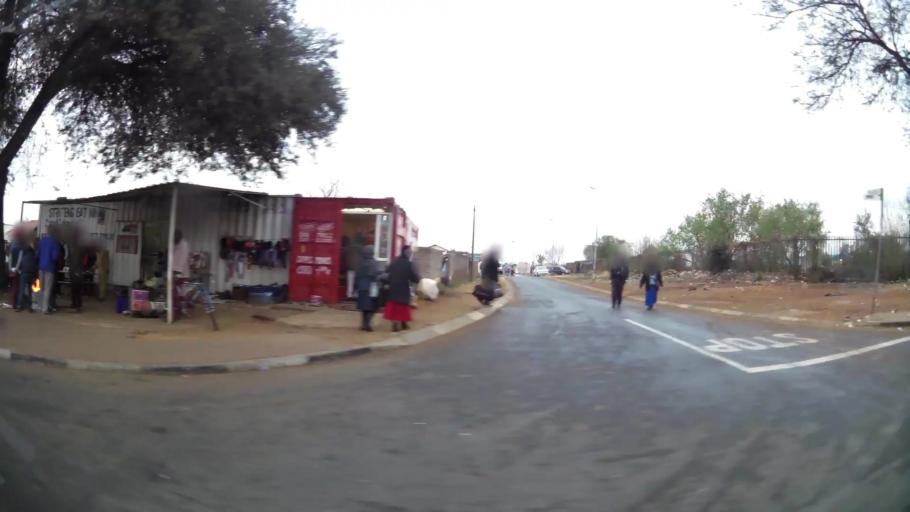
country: ZA
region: Gauteng
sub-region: City of Johannesburg Metropolitan Municipality
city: Soweto
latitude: -26.2453
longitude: 27.8736
